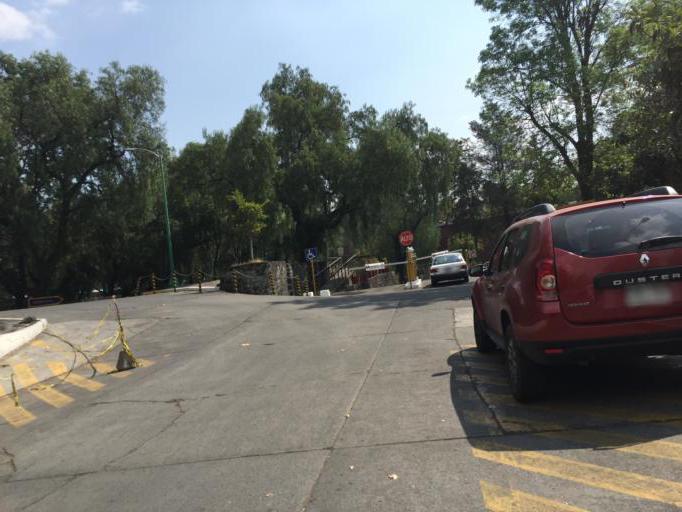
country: MX
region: Mexico City
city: Coyoacan
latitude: 19.3303
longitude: -99.1831
